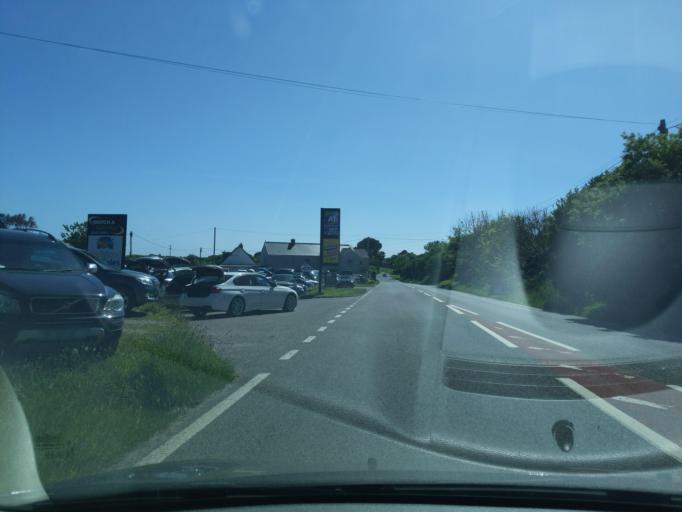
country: GB
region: England
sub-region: Cornwall
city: Wendron
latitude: 50.1240
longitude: -5.2371
